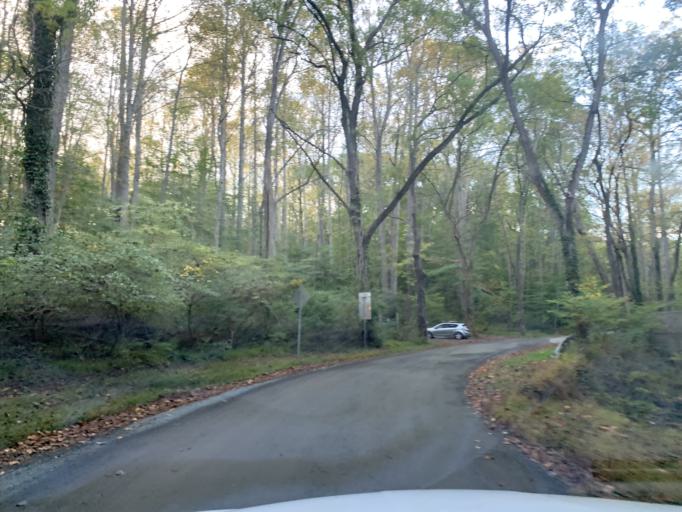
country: US
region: Maryland
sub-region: Harford County
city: Fallston
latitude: 39.5065
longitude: -76.4288
